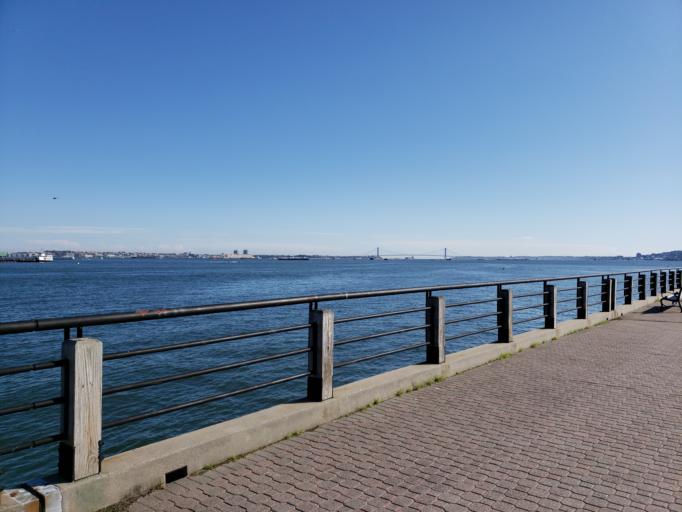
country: US
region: New Jersey
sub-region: Hudson County
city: Jersey City
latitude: 40.6943
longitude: -74.0527
